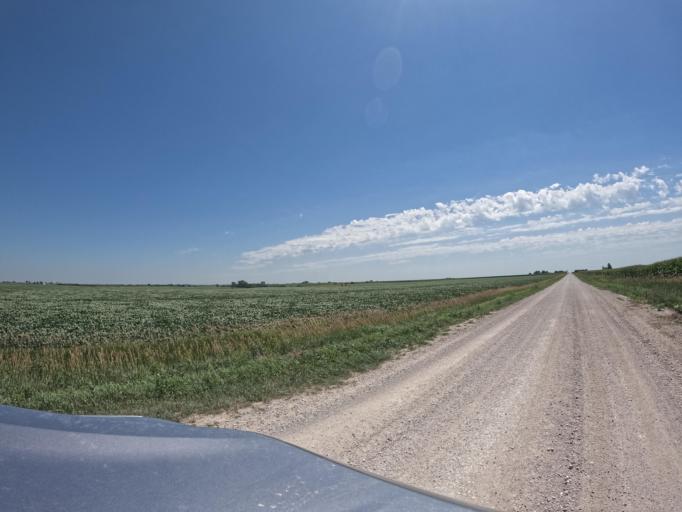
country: US
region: Iowa
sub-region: Keokuk County
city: Sigourney
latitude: 41.4495
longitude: -92.3357
